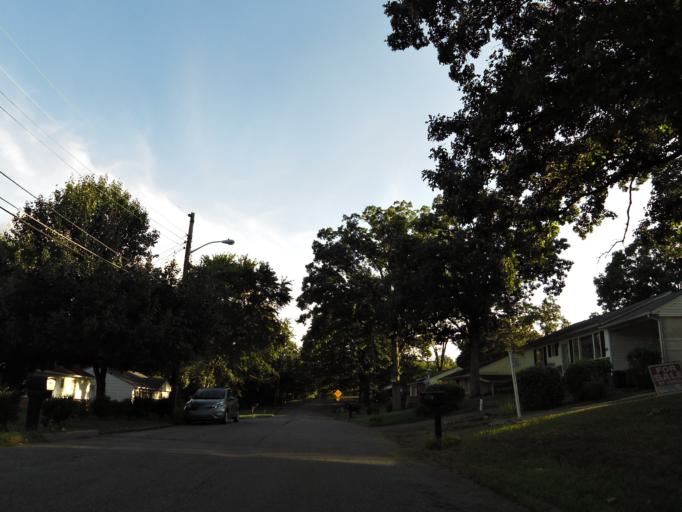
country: US
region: Tennessee
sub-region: Knox County
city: Knoxville
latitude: 36.0040
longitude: -83.9329
